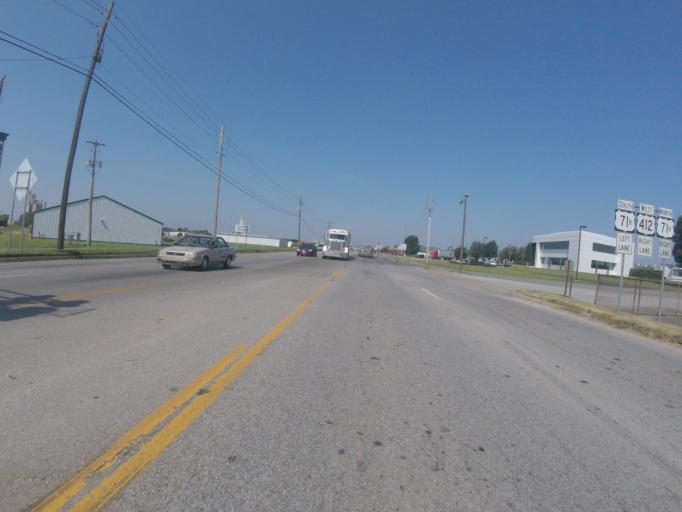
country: US
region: Arkansas
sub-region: Washington County
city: Springdale
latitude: 36.1673
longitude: -94.1366
